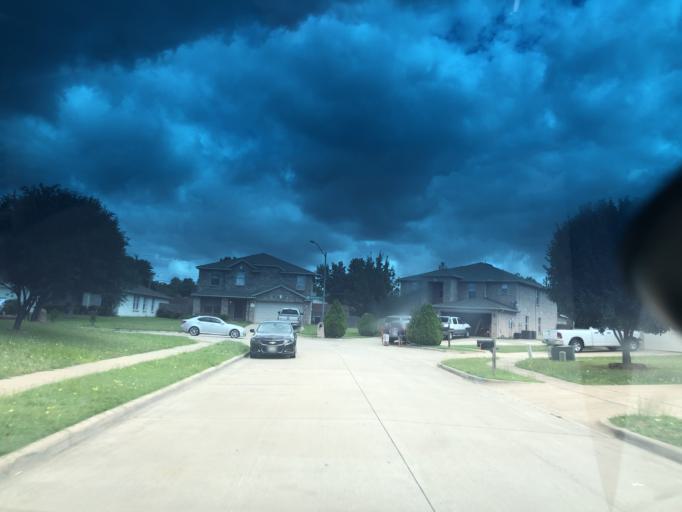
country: US
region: Texas
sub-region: Dallas County
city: Grand Prairie
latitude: 32.7053
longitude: -97.0386
